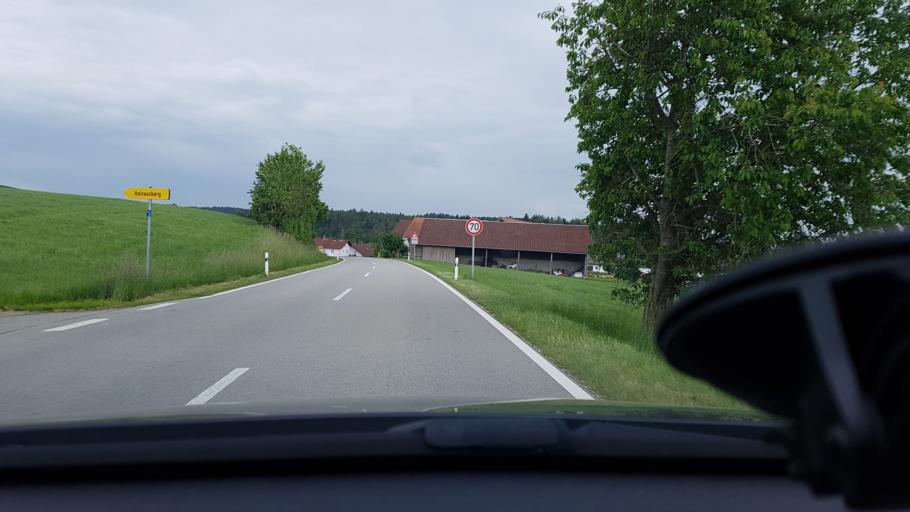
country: DE
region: Bavaria
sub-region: Lower Bavaria
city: Triftern
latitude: 48.3619
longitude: 13.0071
